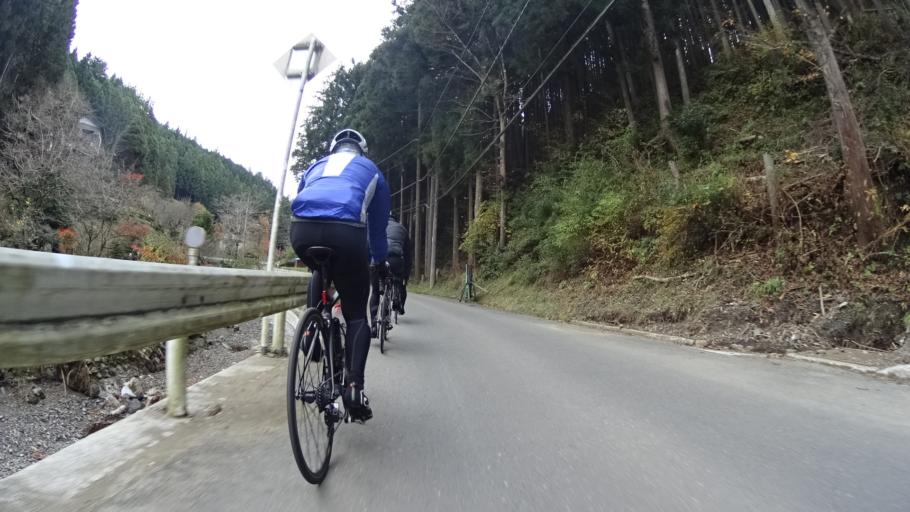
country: JP
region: Saitama
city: Morohongo
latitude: 35.9253
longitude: 139.1896
